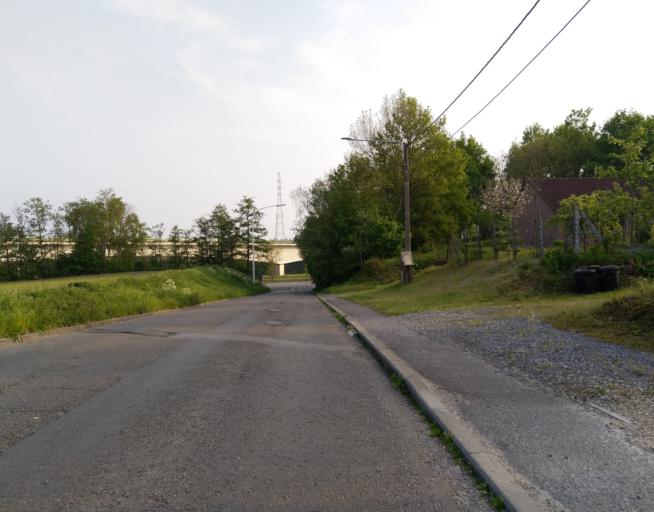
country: BE
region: Wallonia
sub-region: Province du Hainaut
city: Roeulx
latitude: 50.4728
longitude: 4.0363
